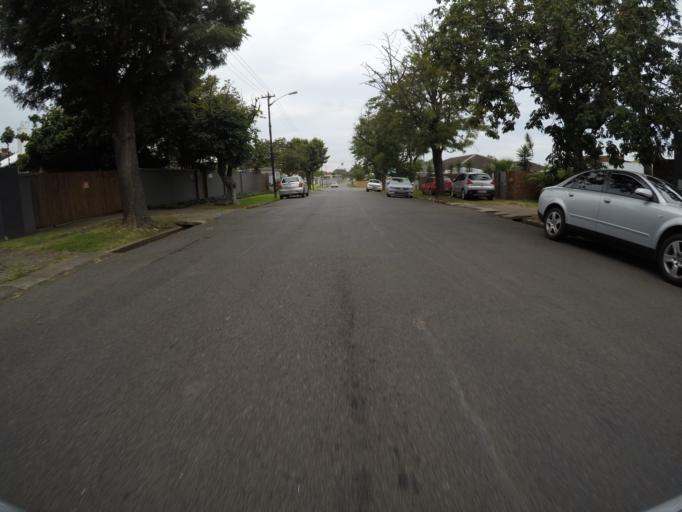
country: ZA
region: Eastern Cape
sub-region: Buffalo City Metropolitan Municipality
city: East London
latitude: -32.9812
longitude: 27.9040
